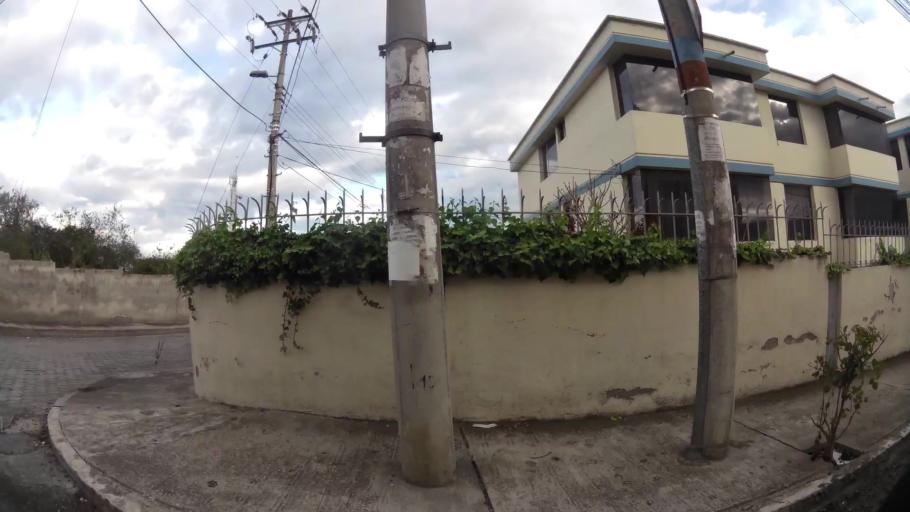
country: EC
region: Pichincha
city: Quito
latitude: -0.1485
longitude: -78.4621
